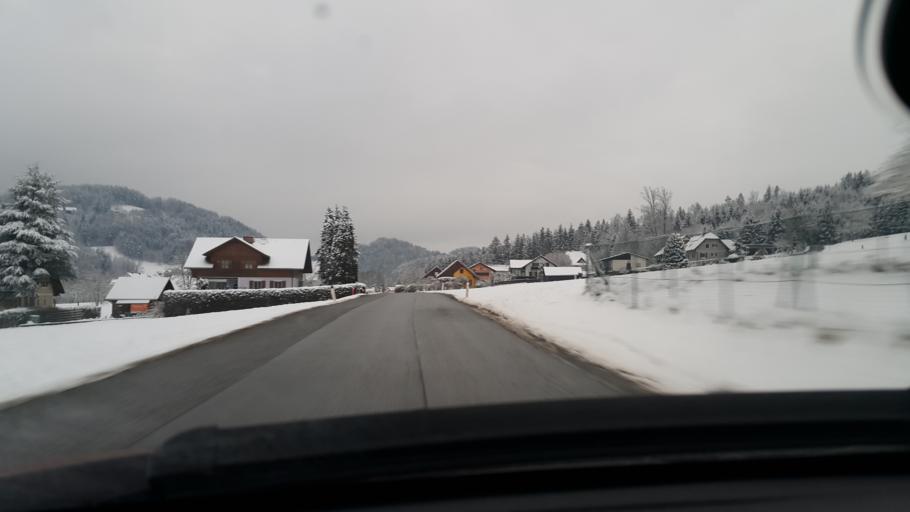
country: AT
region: Styria
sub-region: Politischer Bezirk Graz-Umgebung
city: Sankt Oswald bei Plankenwarth
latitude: 47.0773
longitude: 15.2633
